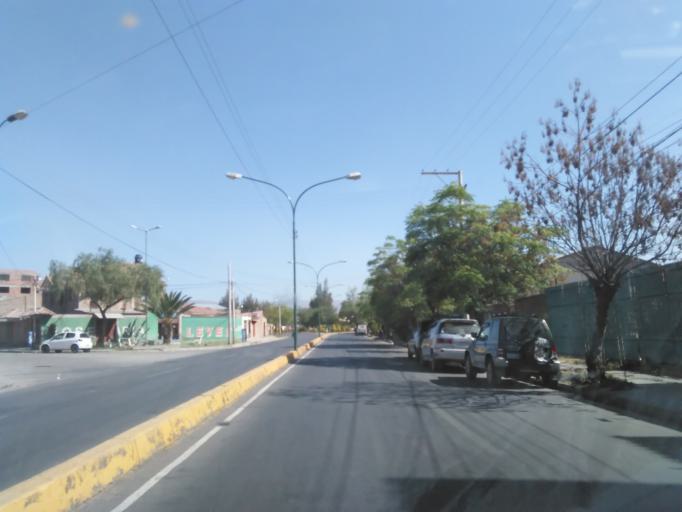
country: BO
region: Cochabamba
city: Cochabamba
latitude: -17.4138
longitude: -66.1609
